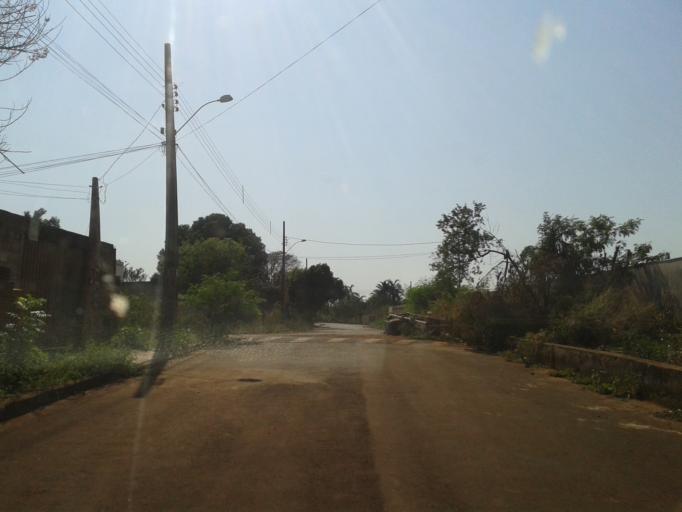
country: BR
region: Minas Gerais
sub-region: Ituiutaba
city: Ituiutaba
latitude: -18.9639
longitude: -49.4809
